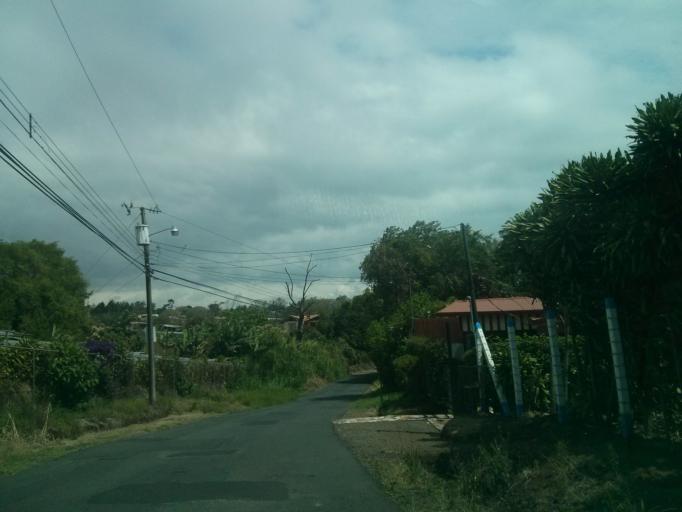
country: CR
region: Heredia
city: Angeles
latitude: 10.0172
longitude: -84.0343
